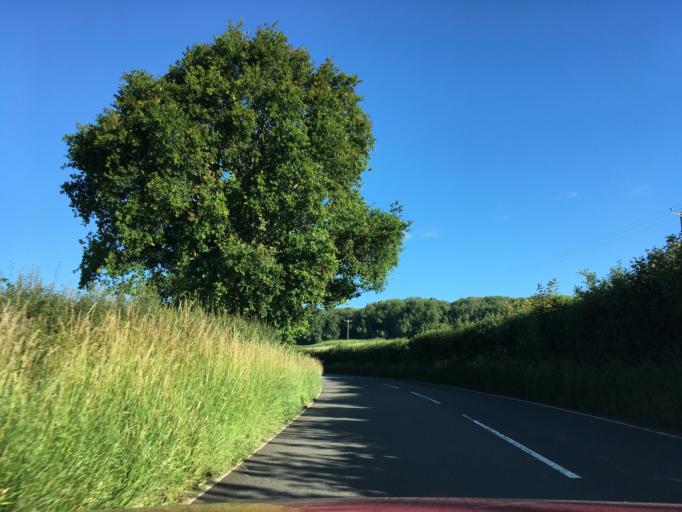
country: GB
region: Wales
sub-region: Monmouthshire
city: Chepstow
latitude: 51.6587
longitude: -2.7264
